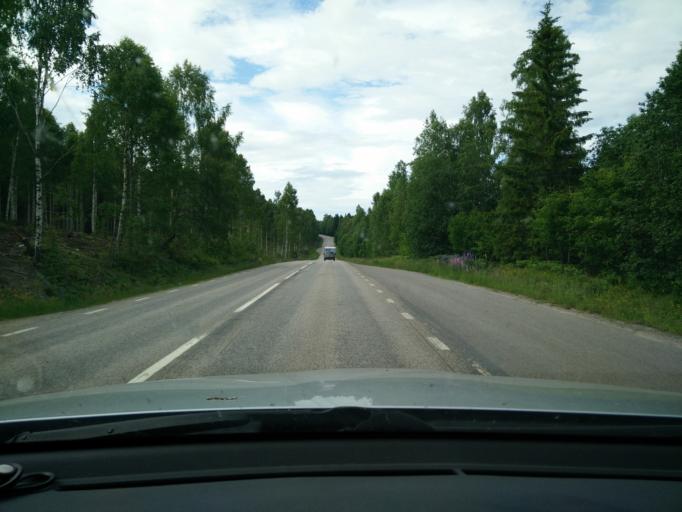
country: SE
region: Gaevleborg
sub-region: Nordanstigs Kommun
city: Bergsjoe
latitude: 61.9625
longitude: 17.0617
